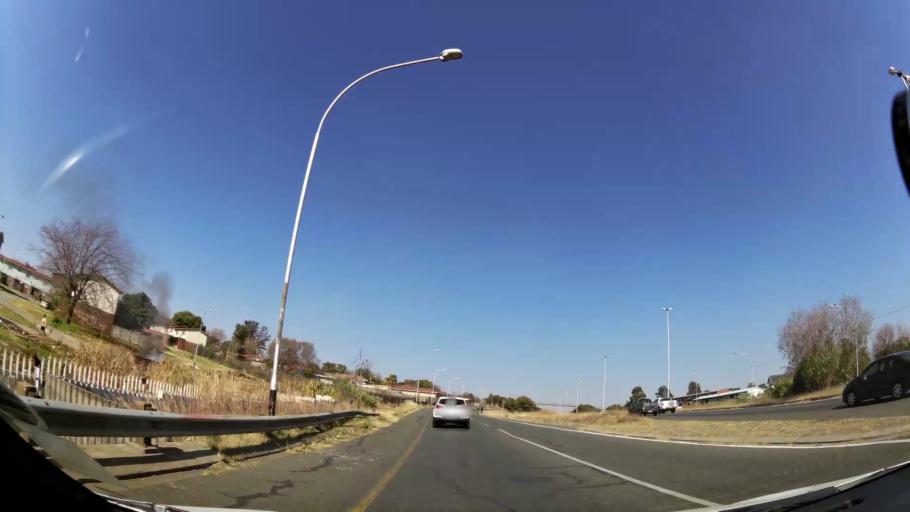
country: ZA
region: Gauteng
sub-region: City of Johannesburg Metropolitan Municipality
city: Johannesburg
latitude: -26.2557
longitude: 28.0288
